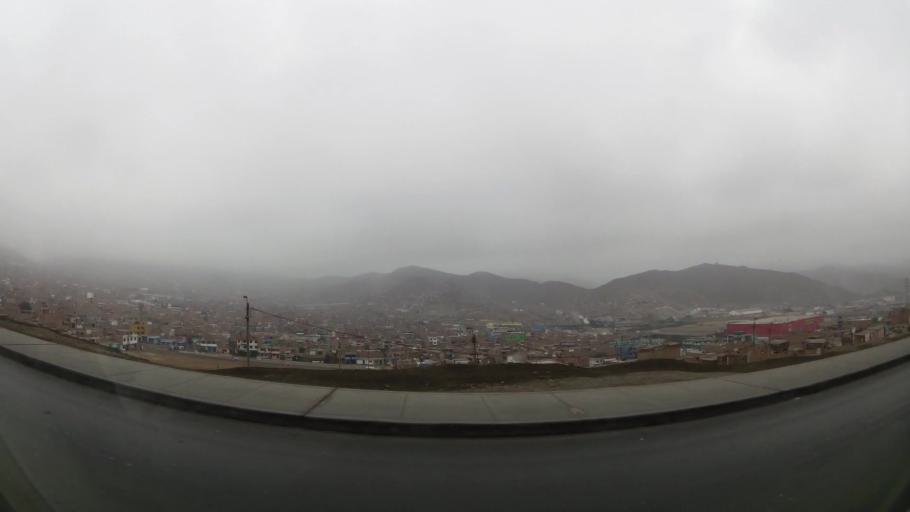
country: PE
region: Lima
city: Ventanilla
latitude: -11.8587
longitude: -77.1304
